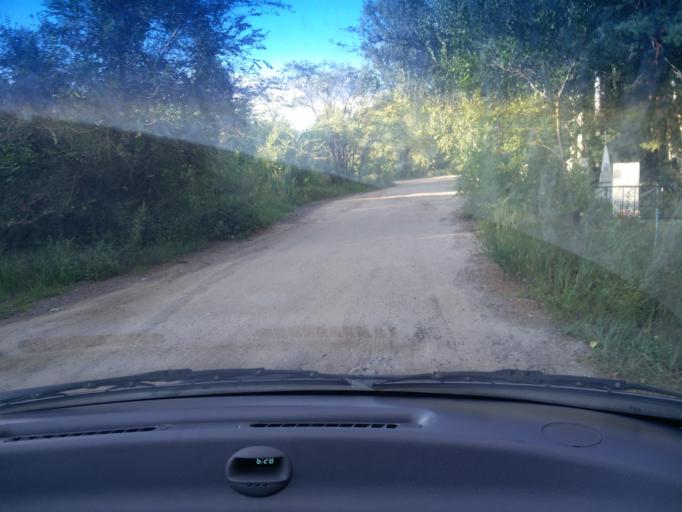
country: RU
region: Voronezj
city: Pridonskoy
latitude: 51.6733
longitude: 39.1093
